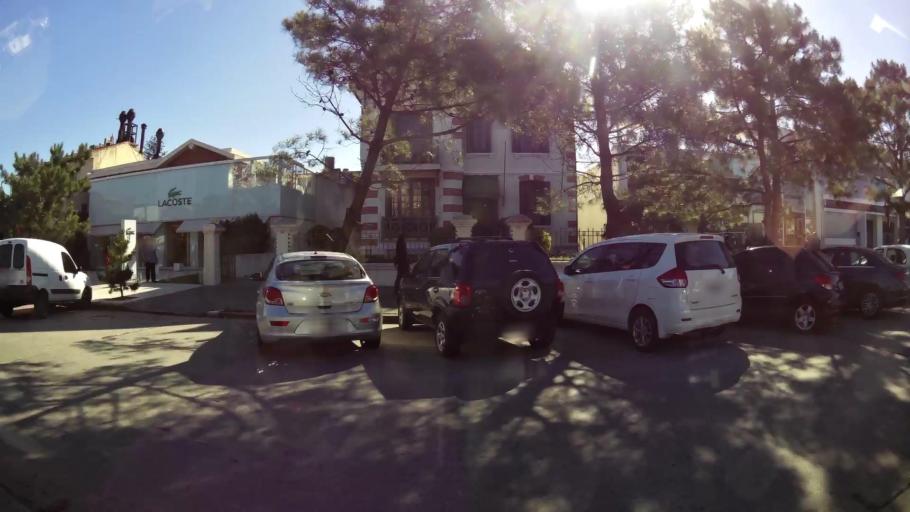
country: UY
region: Canelones
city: Paso de Carrasco
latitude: -34.8885
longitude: -56.0576
